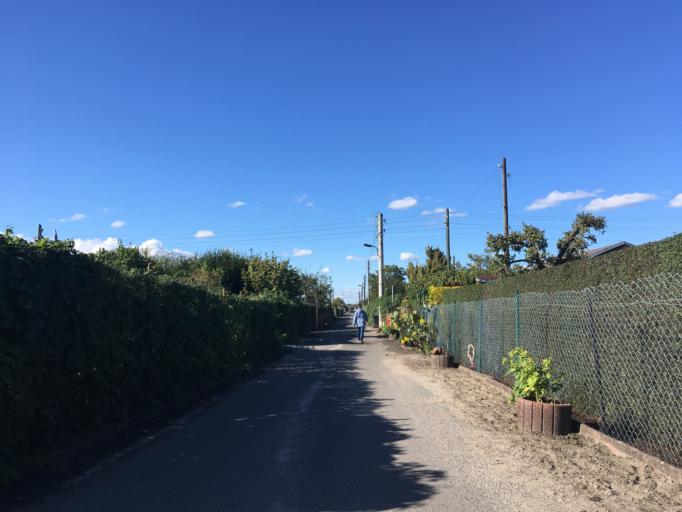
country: DE
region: Berlin
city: Buchholz
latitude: 52.6131
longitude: 13.4205
